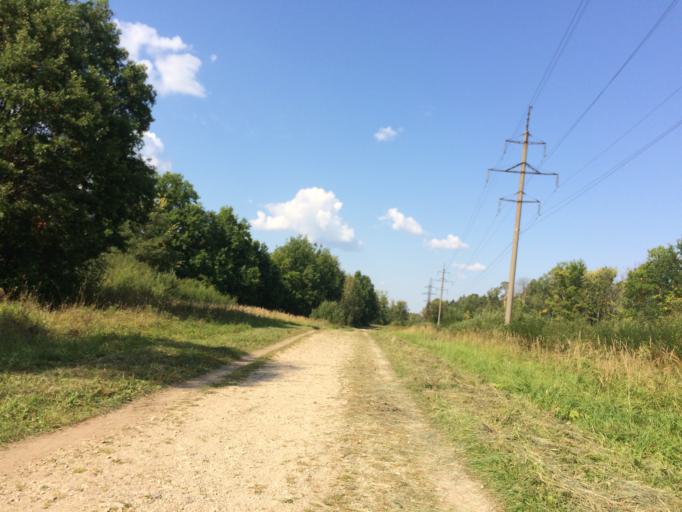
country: RU
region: Mariy-El
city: Yoshkar-Ola
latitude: 56.6154
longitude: 47.9315
